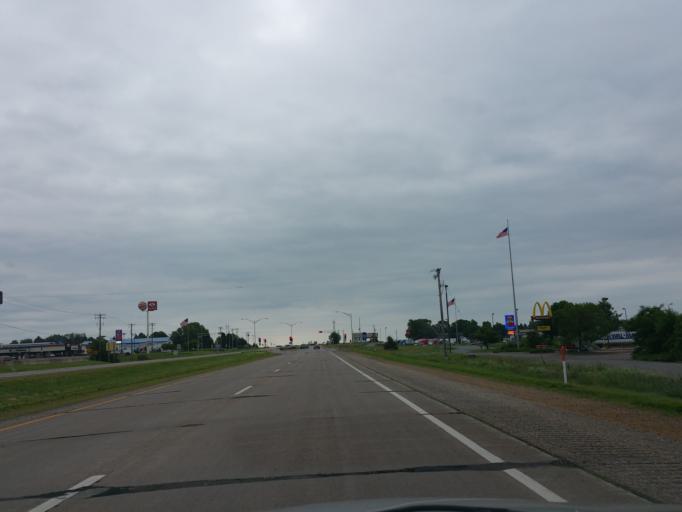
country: US
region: Wisconsin
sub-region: Eau Claire County
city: Eau Claire
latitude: 44.8434
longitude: -91.5973
